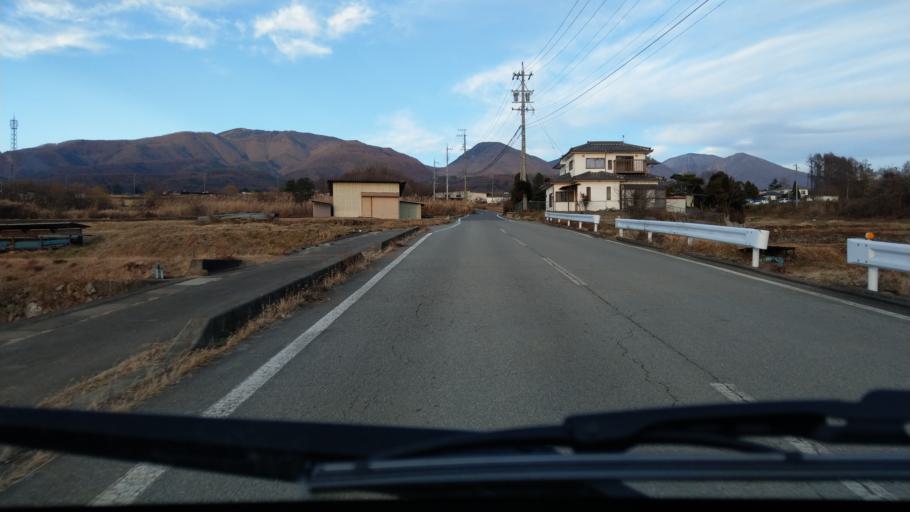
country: JP
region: Nagano
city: Komoro
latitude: 36.3484
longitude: 138.3944
